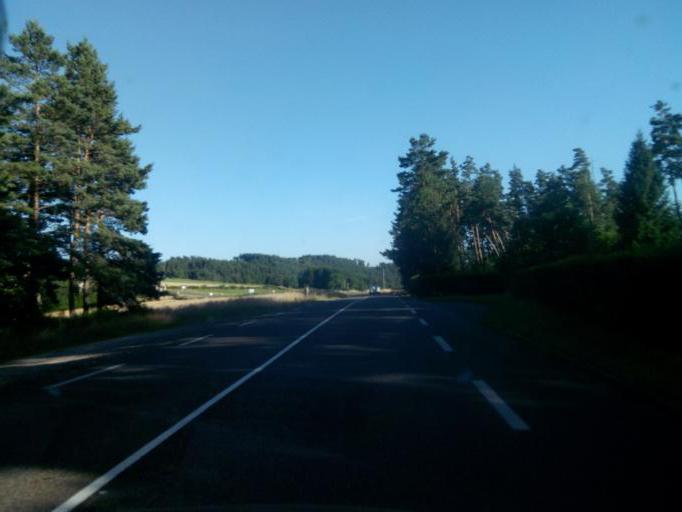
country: FR
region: Rhone-Alpes
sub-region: Departement de la Loire
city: Usson-en-Forez
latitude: 45.3581
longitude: 3.9002
